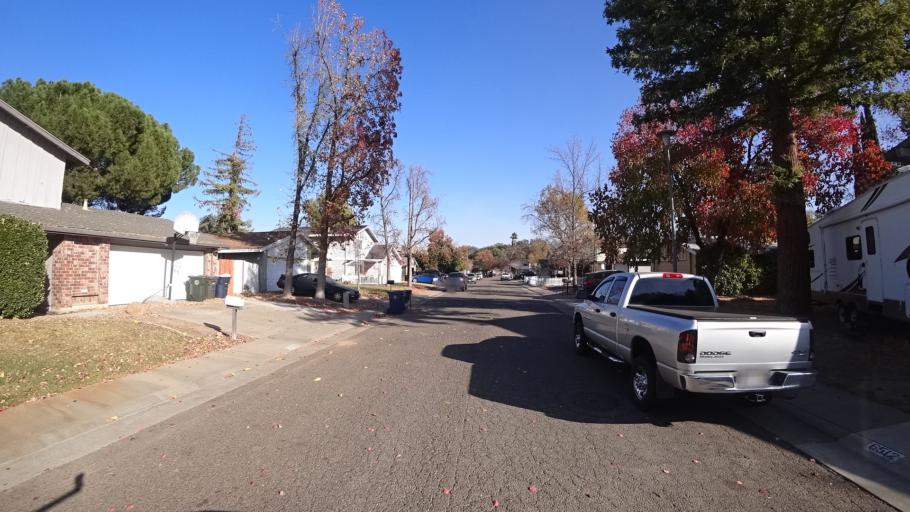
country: US
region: California
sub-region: Sacramento County
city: Antelope
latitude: 38.6967
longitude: -121.3116
